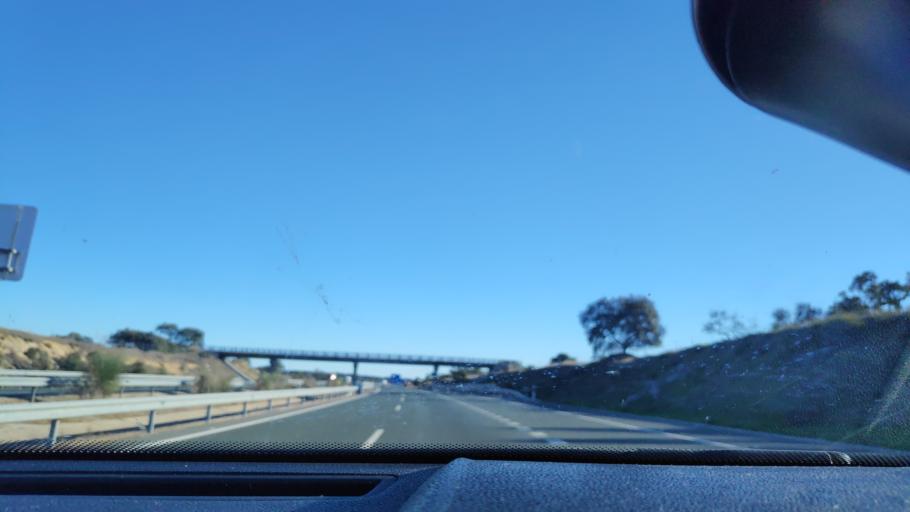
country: ES
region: Andalusia
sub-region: Provincia de Huelva
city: Santa Olalla del Cala
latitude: 37.9171
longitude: -6.2224
